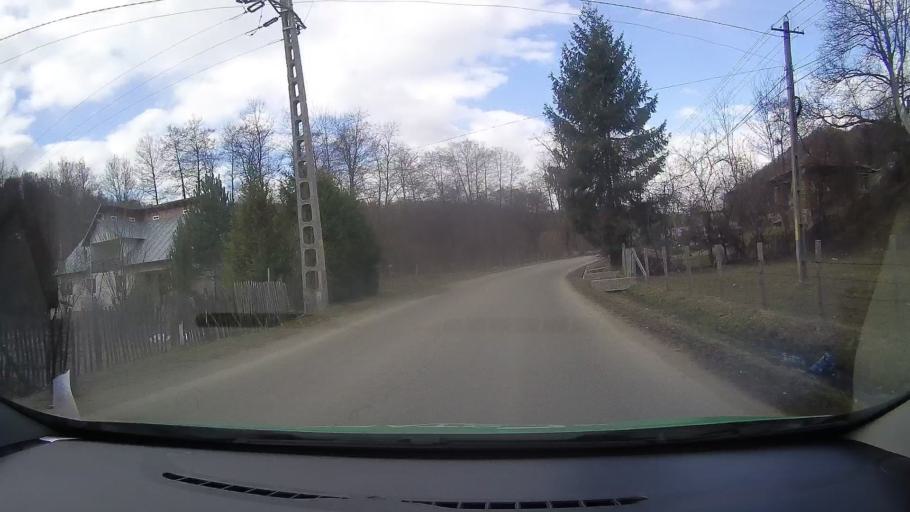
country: RO
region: Dambovita
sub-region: Comuna Varfuri
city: Varfuri
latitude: 45.0766
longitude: 25.5226
